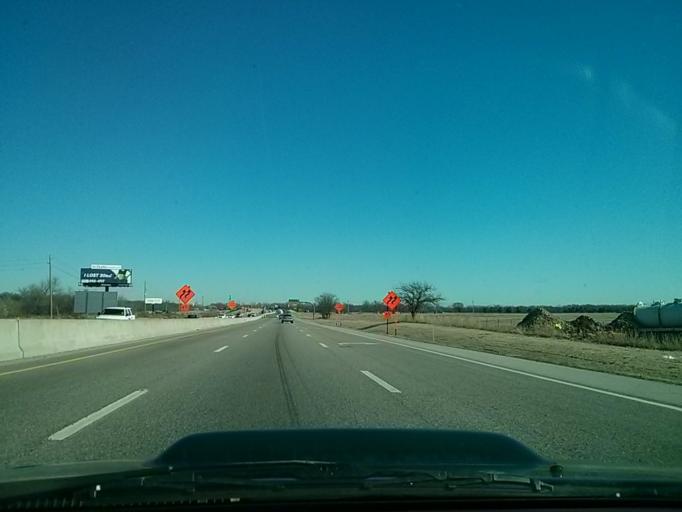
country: US
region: Oklahoma
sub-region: Tulsa County
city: Owasso
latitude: 36.2285
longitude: -95.8504
